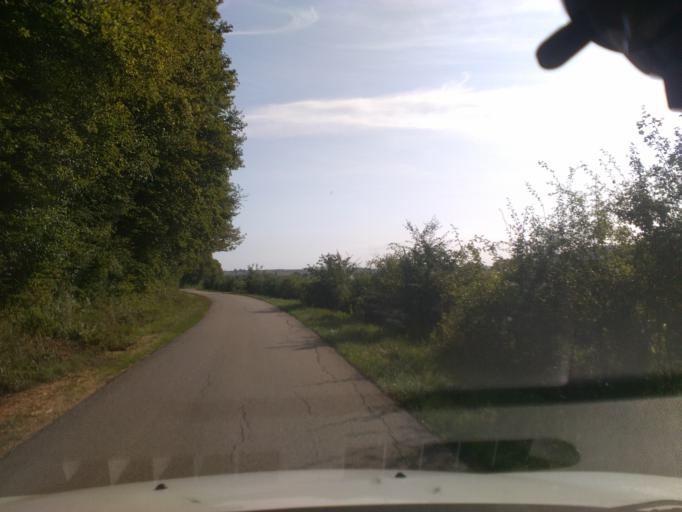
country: FR
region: Lorraine
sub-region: Departement des Vosges
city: Mirecourt
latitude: 48.3008
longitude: 6.0277
